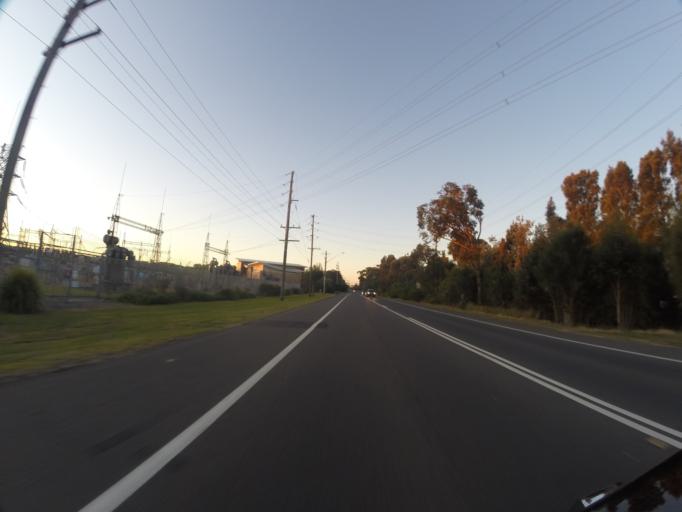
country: AU
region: New South Wales
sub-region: Sutherland Shire
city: Kurnell
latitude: -34.0162
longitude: 151.2063
